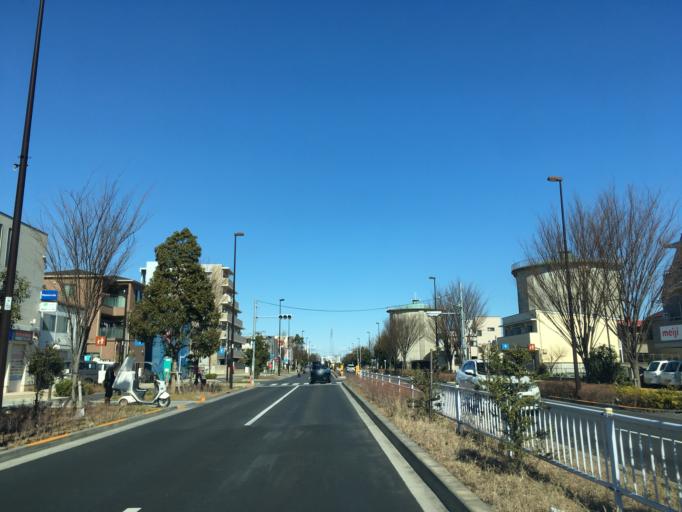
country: JP
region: Tokyo
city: Mitaka-shi
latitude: 35.6855
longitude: 139.5499
